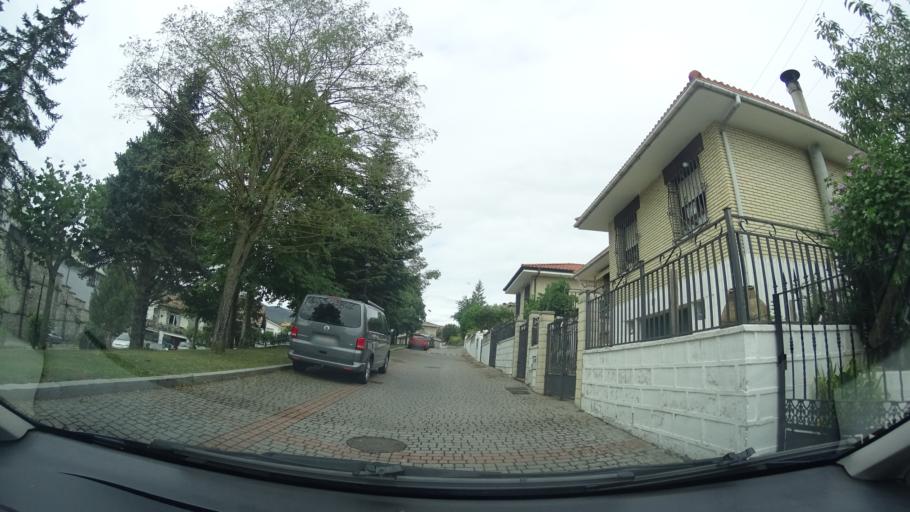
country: ES
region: Basque Country
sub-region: Provincia de Alava
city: Arminon
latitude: 42.8187
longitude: -2.8081
